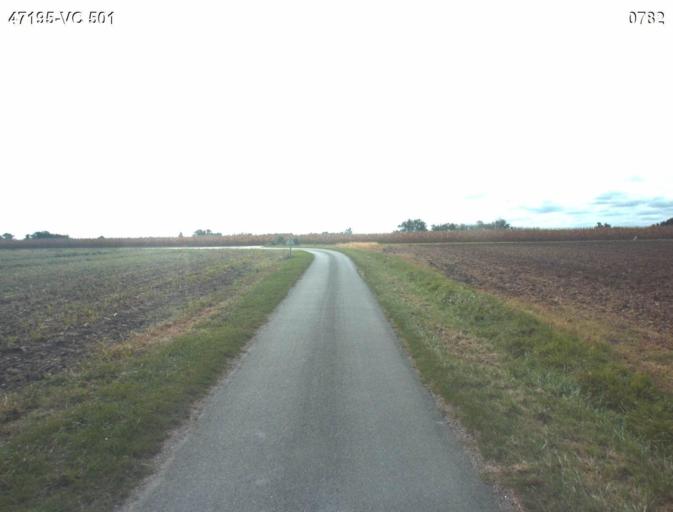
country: FR
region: Aquitaine
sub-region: Departement du Lot-et-Garonne
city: Nerac
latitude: 44.1016
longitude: 0.3180
